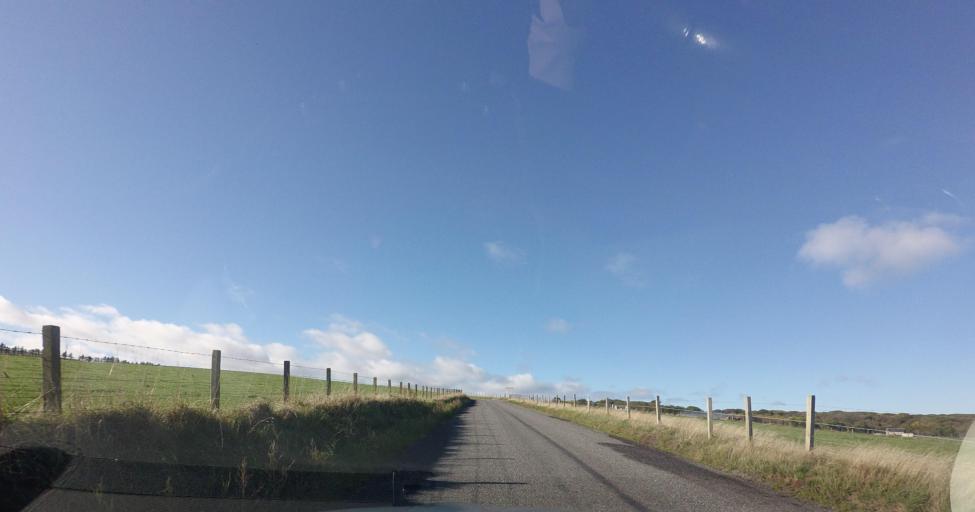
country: GB
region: Scotland
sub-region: Aberdeenshire
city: Rosehearty
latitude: 57.6794
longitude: -2.2775
